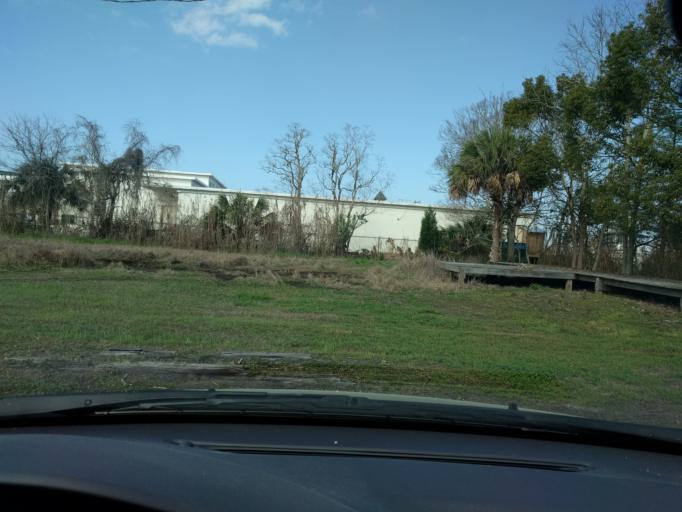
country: US
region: Florida
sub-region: Franklin County
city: Apalachicola
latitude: 29.7322
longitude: -84.9890
